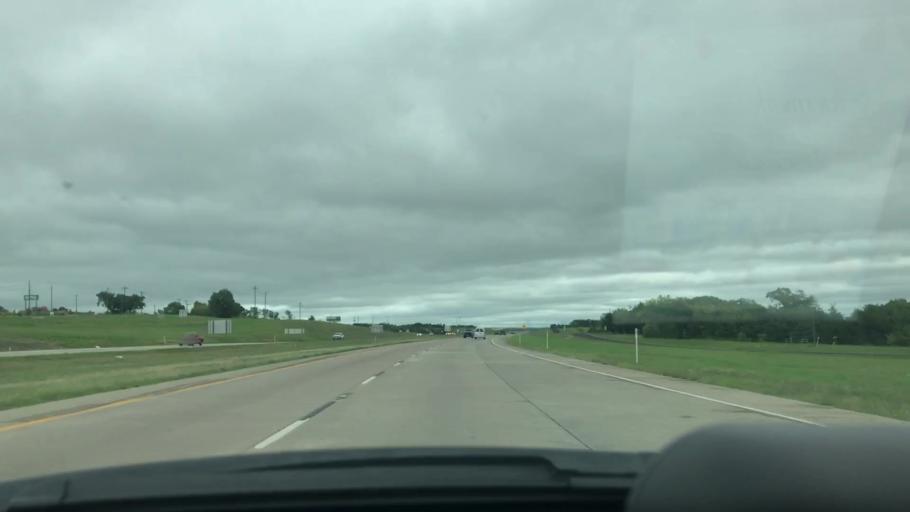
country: US
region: Texas
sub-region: Grayson County
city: Sherman
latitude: 33.6814
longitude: -96.6074
